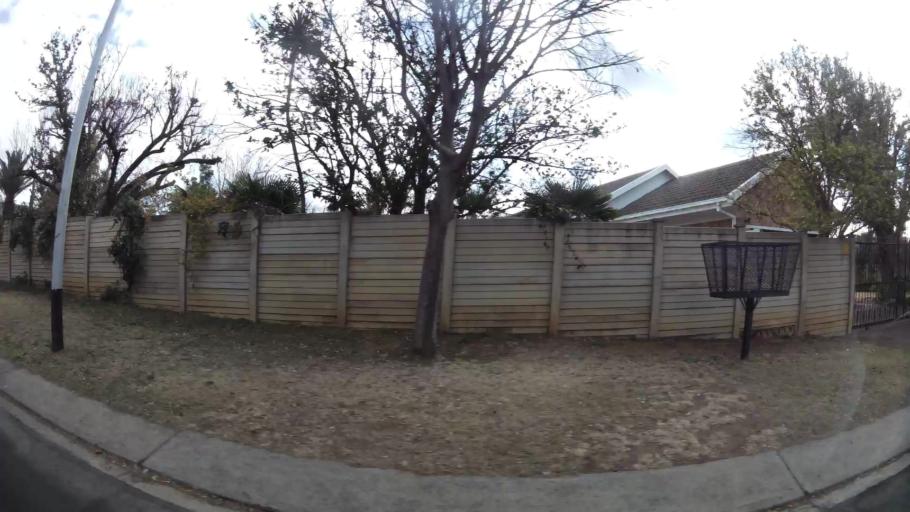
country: ZA
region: Orange Free State
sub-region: Mangaung Metropolitan Municipality
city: Bloemfontein
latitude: -29.0741
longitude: 26.2125
